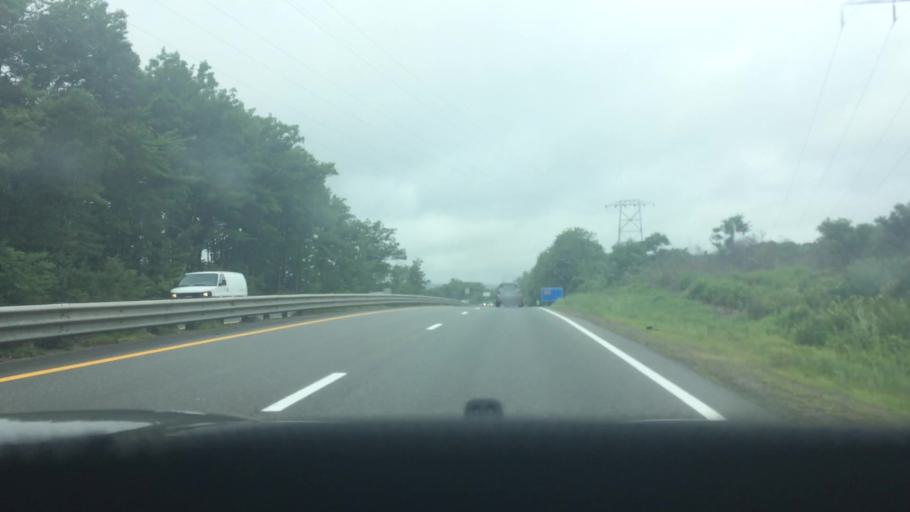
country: US
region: Massachusetts
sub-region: Worcester County
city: Fitchburg
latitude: 42.5475
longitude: -71.8242
